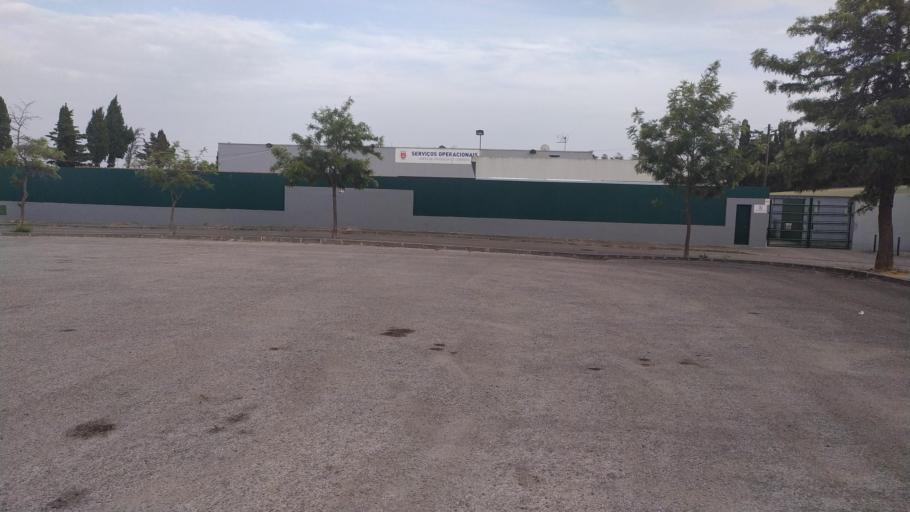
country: PT
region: Setubal
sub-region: Seixal
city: Corroios
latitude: 38.6243
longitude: -9.1487
